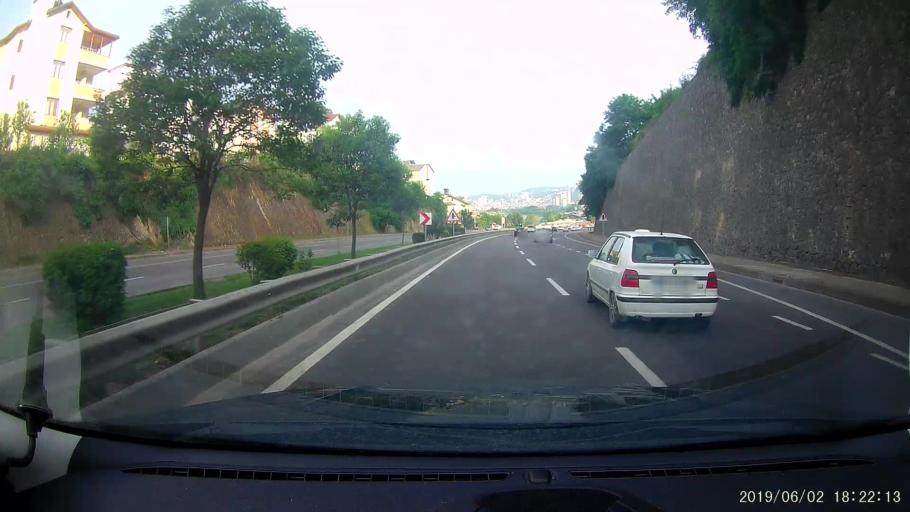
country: TR
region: Ordu
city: Fatsa
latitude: 41.0598
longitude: 37.4761
